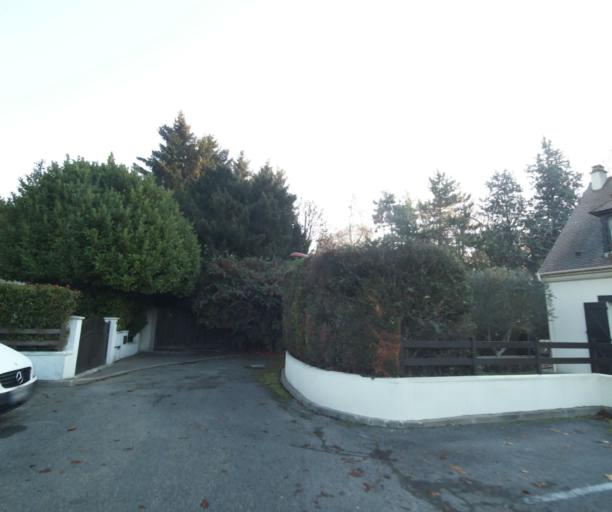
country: FR
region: Ile-de-France
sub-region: Departement du Val-d'Oise
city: Gonesse
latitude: 48.9842
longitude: 2.4451
